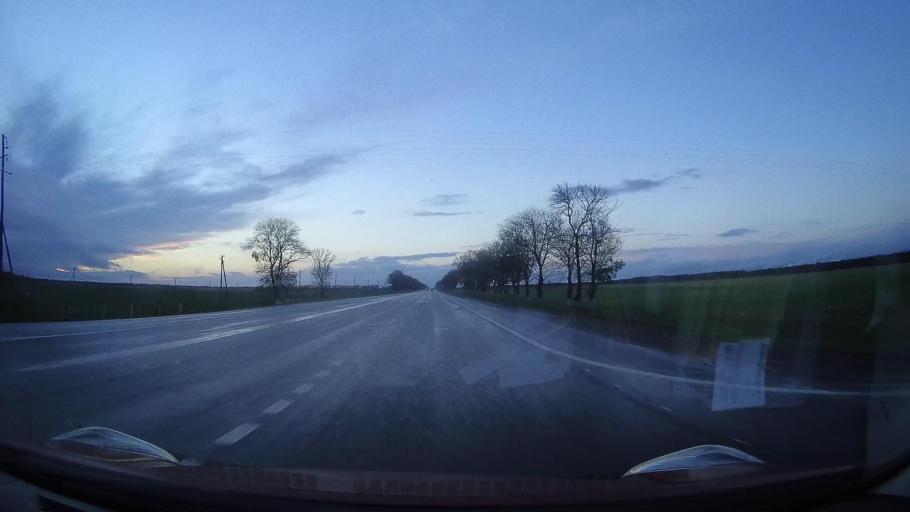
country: RU
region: Krasnodarskiy
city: Uspenskoye
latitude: 44.8161
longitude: 41.3750
